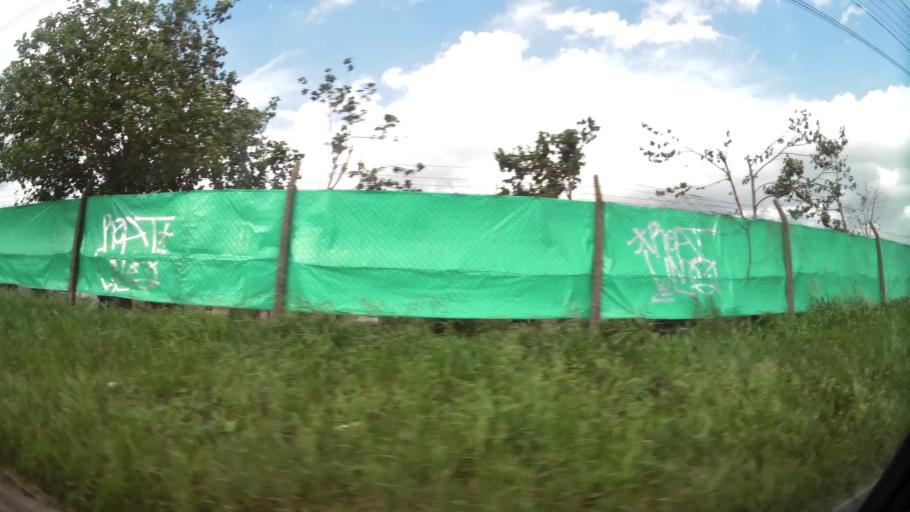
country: AR
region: Buenos Aires
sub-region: Partido de Tigre
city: Tigre
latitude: -34.4738
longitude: -58.6569
